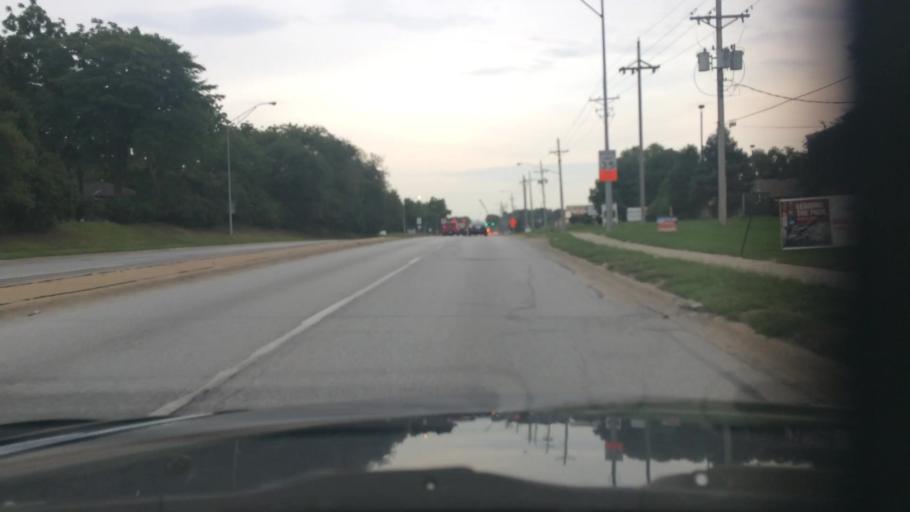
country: US
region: Nebraska
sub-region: Douglas County
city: Ralston
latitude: 41.2050
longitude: -96.0431
